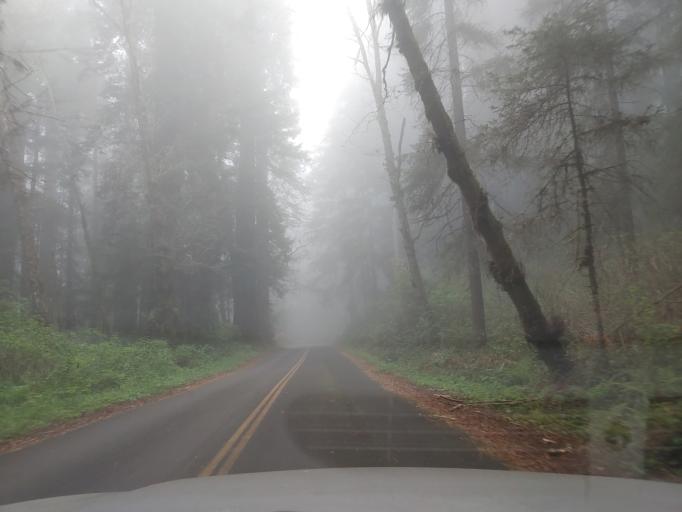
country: US
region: California
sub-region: Del Norte County
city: Bertsch-Oceanview
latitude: 41.4632
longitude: -124.0554
